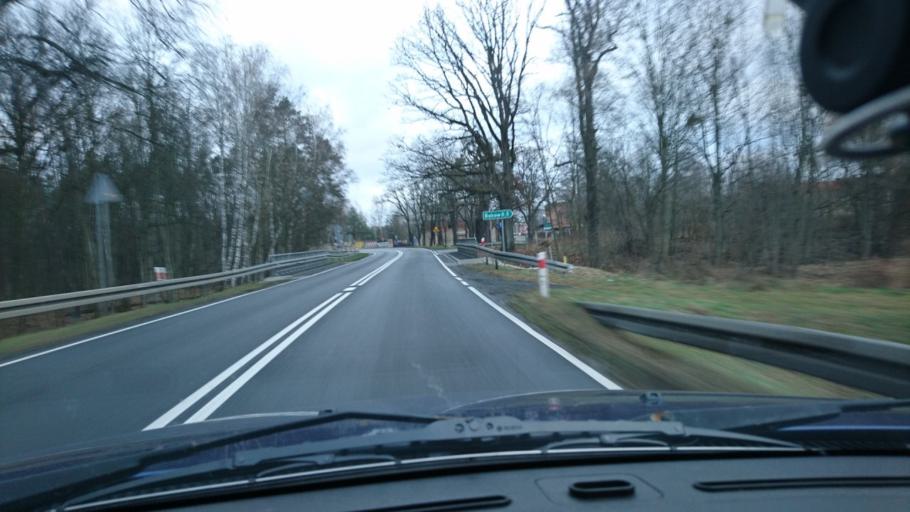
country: PL
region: Opole Voivodeship
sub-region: Powiat kluczborski
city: Kluczbork
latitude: 50.9553
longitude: 18.3087
